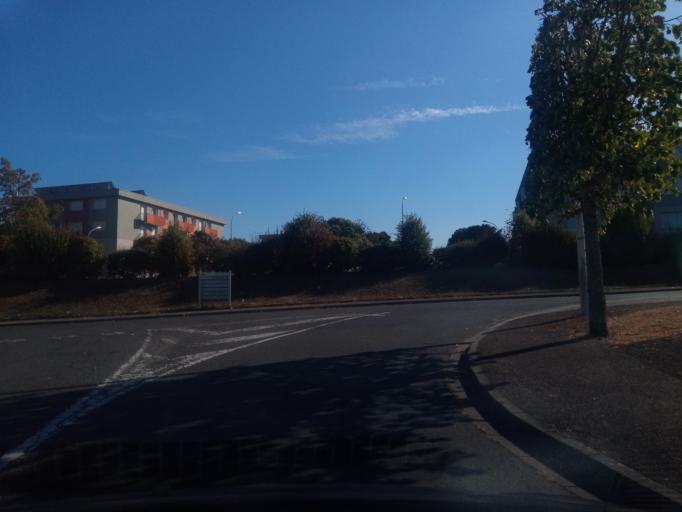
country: FR
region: Poitou-Charentes
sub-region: Departement de la Vienne
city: Montmorillon
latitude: 46.4186
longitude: 0.8538
